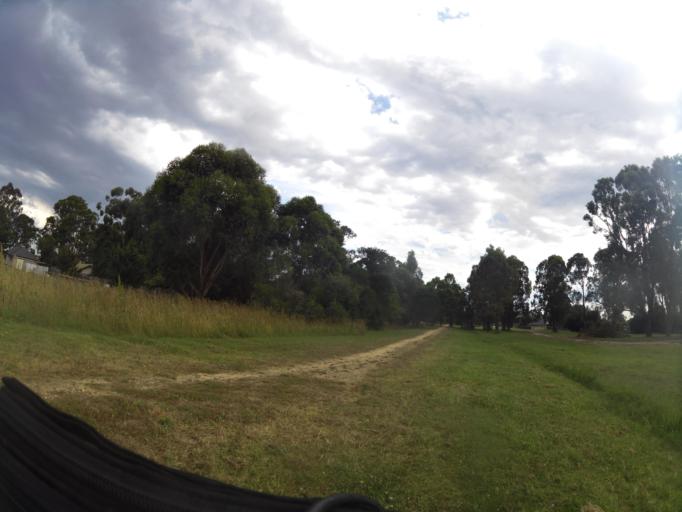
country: AU
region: Victoria
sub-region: Latrobe
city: Traralgon
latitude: -38.0538
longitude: 146.6280
